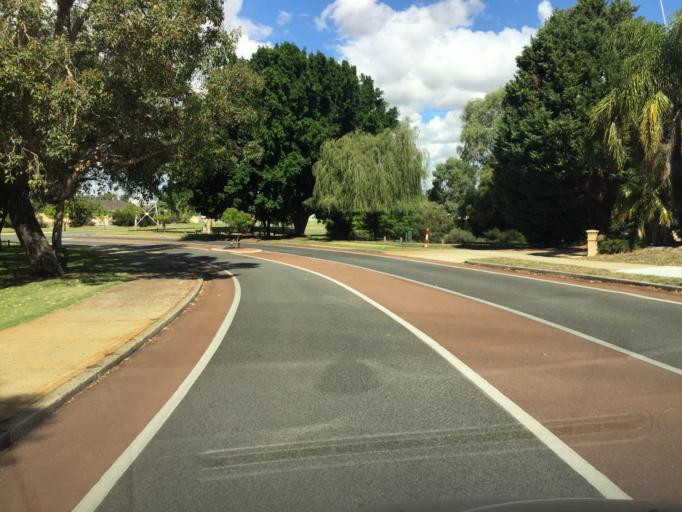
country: AU
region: Western Australia
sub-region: Canning
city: Willetton
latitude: -32.0612
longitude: 115.8934
